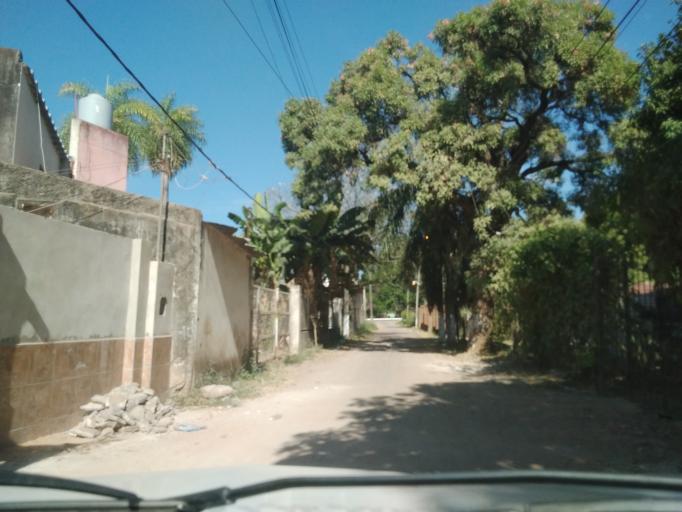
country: AR
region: Corrientes
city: Corrientes
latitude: -27.5144
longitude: -58.8052
